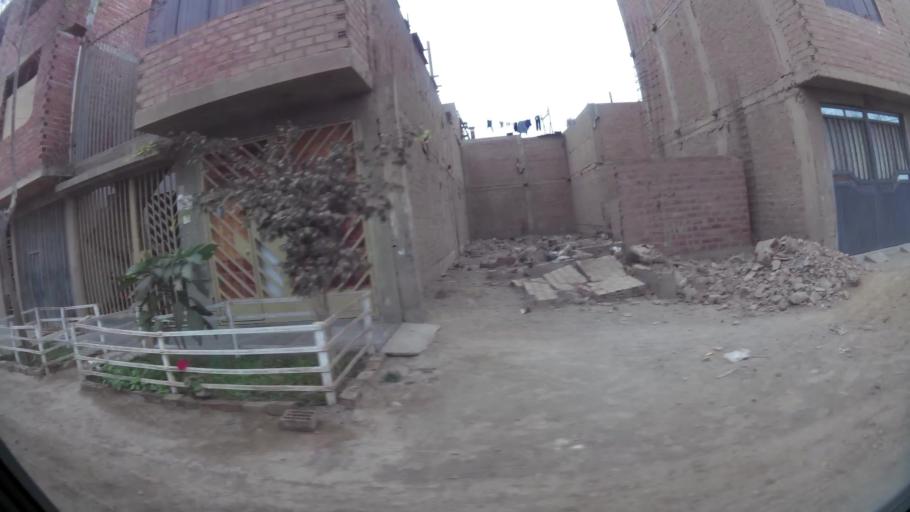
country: PE
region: Lima
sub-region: Lima
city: Independencia
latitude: -11.9659
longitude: -77.0943
